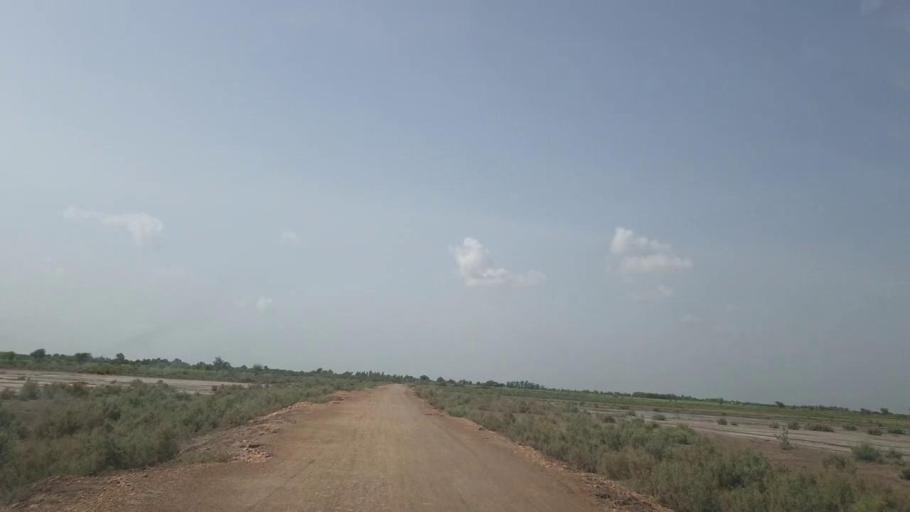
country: PK
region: Sindh
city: Tando Bago
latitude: 24.7730
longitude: 69.1305
